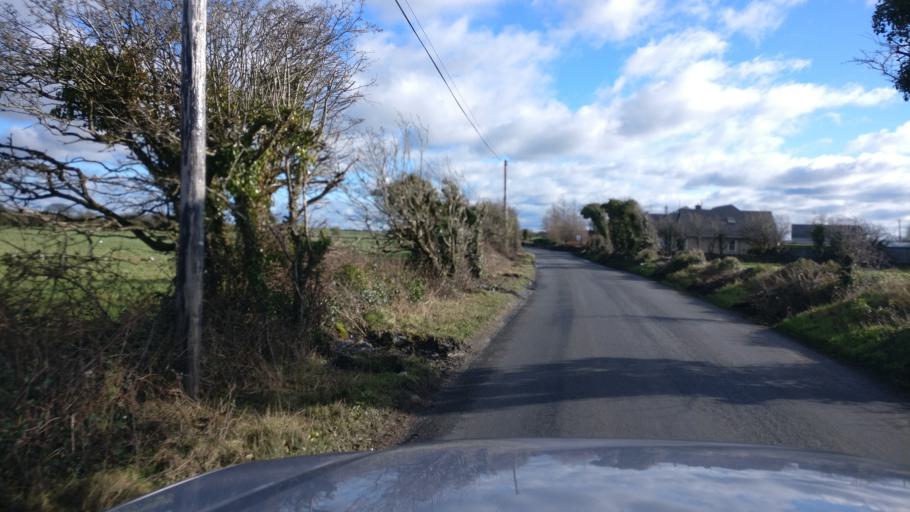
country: IE
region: Connaught
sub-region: County Galway
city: Oranmore
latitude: 53.2728
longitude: -8.8829
